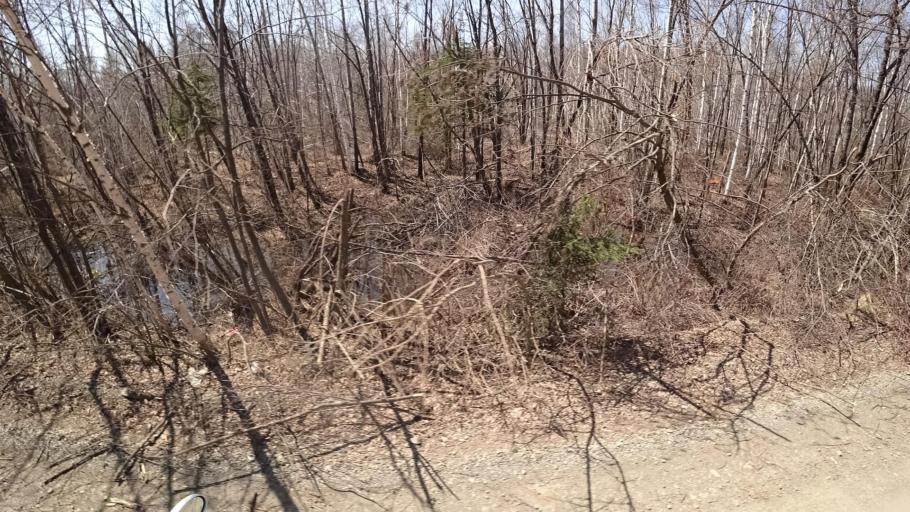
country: RU
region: Khabarovsk Krai
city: Khurba
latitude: 50.4172
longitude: 136.8369
